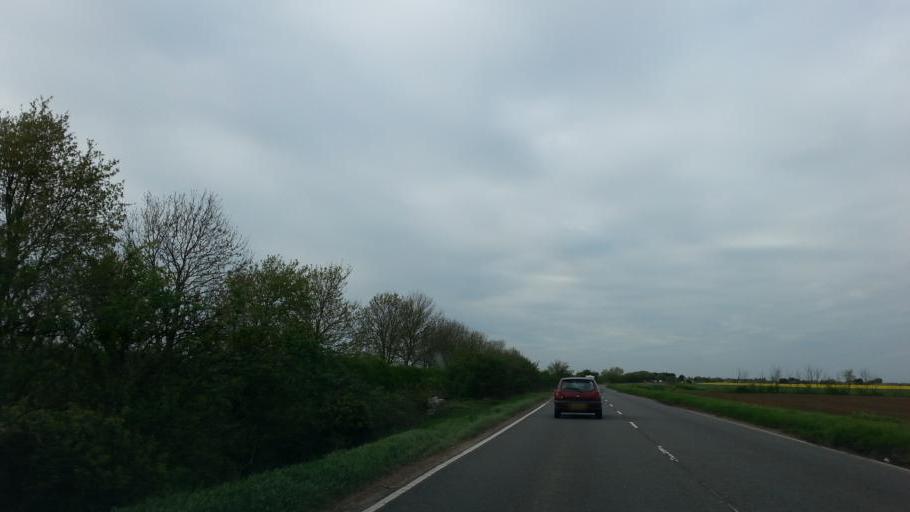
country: GB
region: England
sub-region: Cambridgeshire
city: March
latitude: 52.5760
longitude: 0.0561
